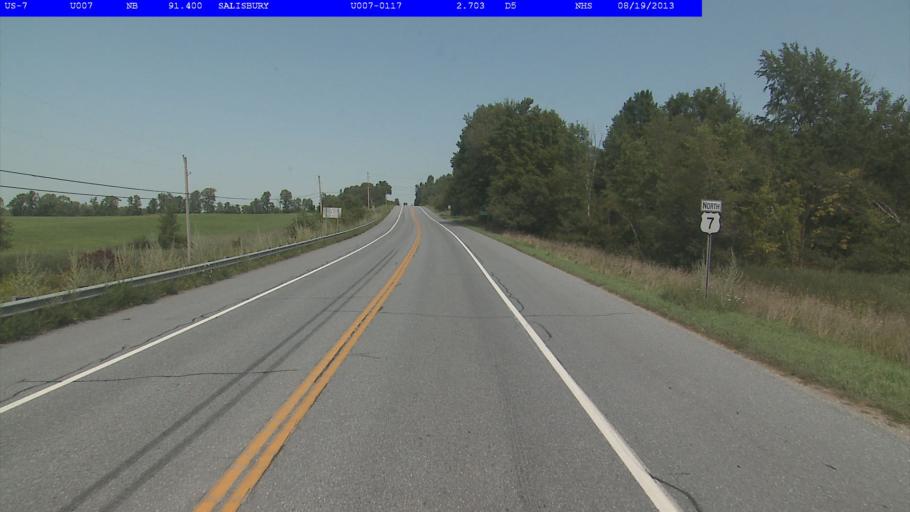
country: US
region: Vermont
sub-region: Addison County
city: Middlebury (village)
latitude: 43.9307
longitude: -73.1088
